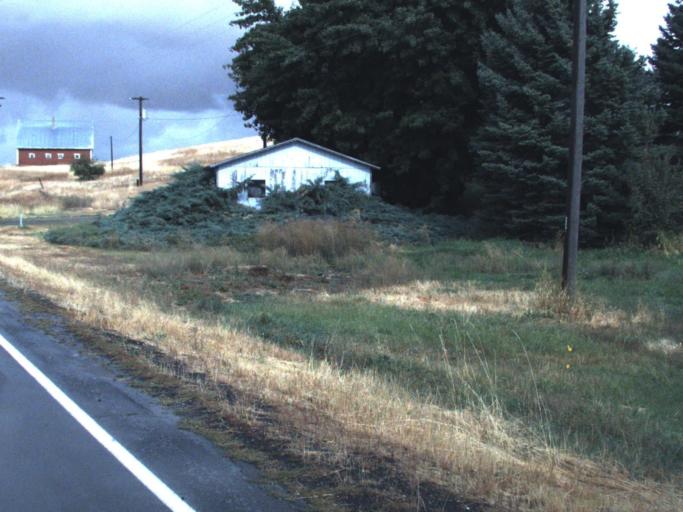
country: US
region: Washington
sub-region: Spokane County
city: Medical Lake
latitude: 47.6875
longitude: -117.8817
